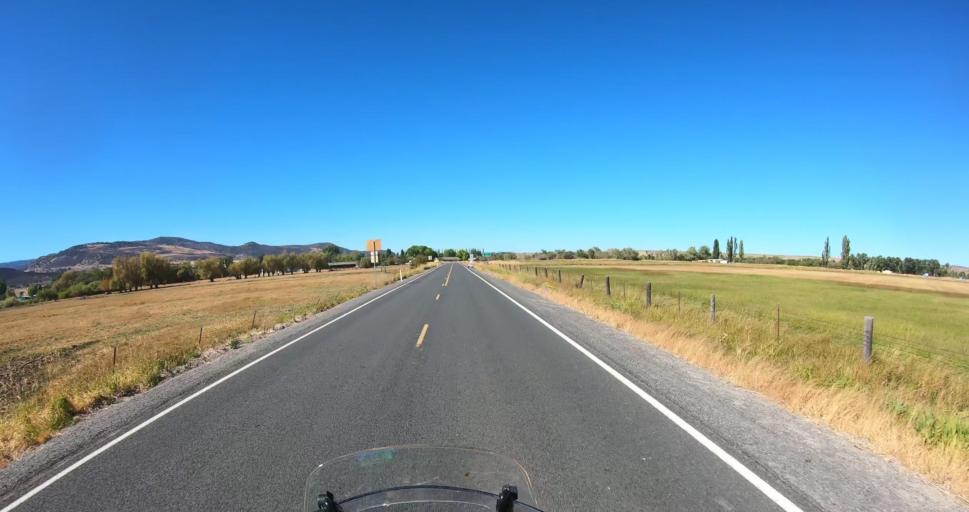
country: US
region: Oregon
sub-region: Lake County
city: Lakeview
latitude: 42.6910
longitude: -120.5355
